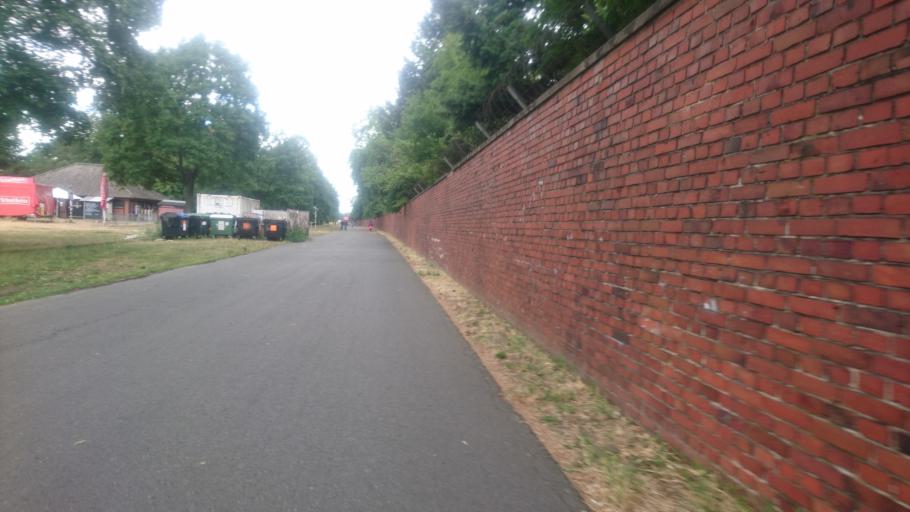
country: DE
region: Berlin
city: Tempelhof Bezirk
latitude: 52.4791
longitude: 13.4105
